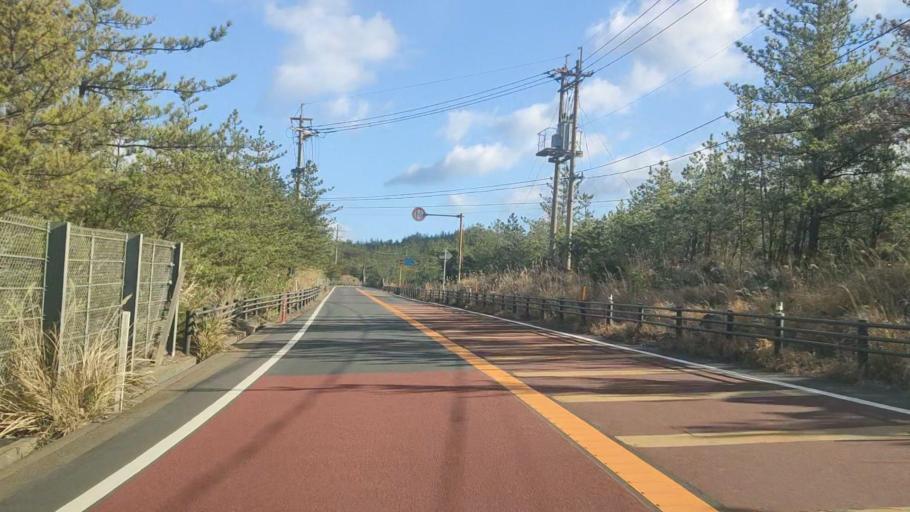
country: JP
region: Kagoshima
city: Tarumizu
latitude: 31.5530
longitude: 130.6726
